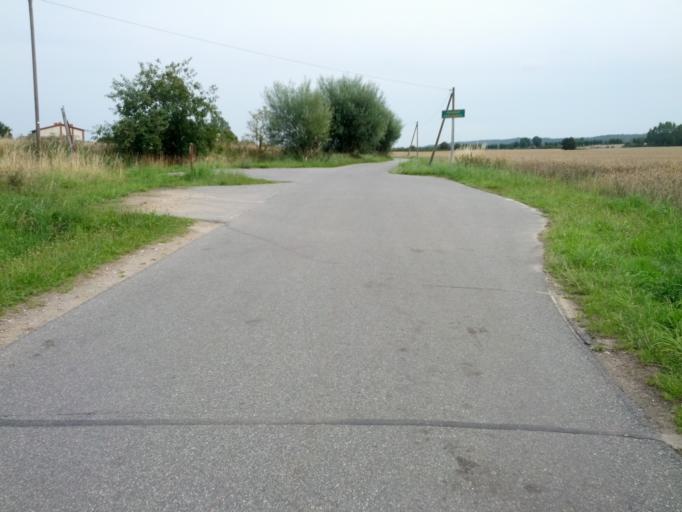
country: DE
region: Mecklenburg-Vorpommern
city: Bastorf
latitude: 54.1493
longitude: 11.6966
